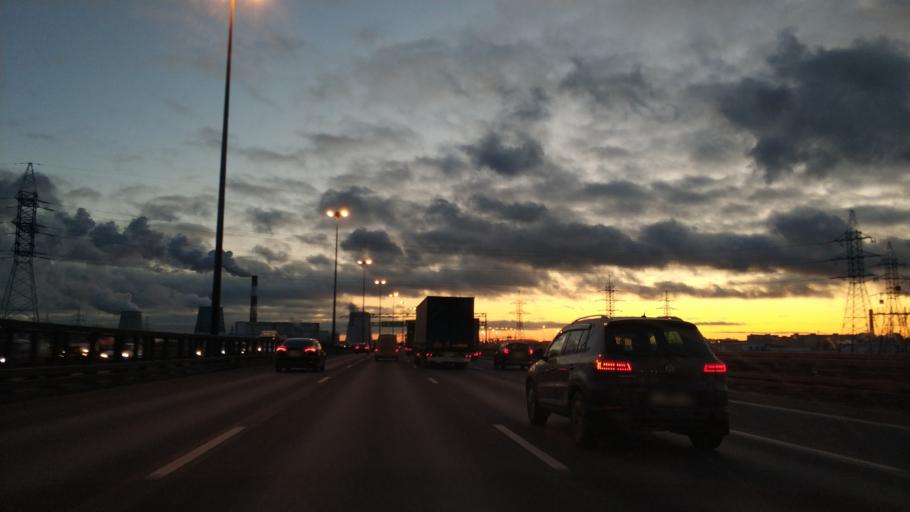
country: RU
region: St.-Petersburg
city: Obukhovo
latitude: 59.8428
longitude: 30.4560
